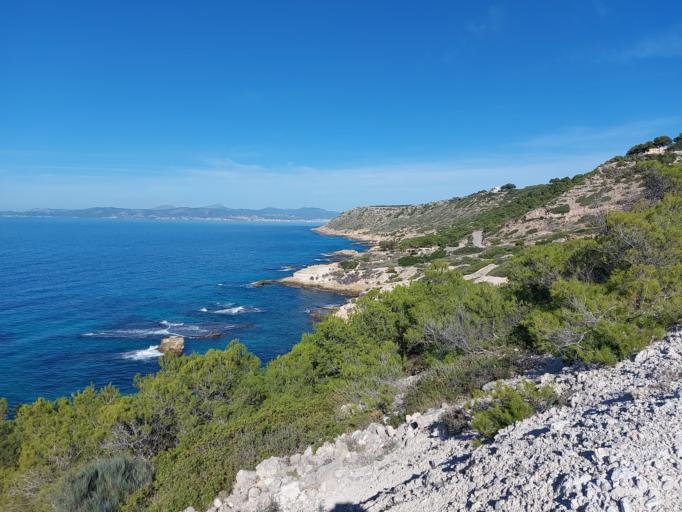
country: ES
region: Balearic Islands
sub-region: Illes Balears
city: s'Arenal
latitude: 39.4477
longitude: 2.7446
